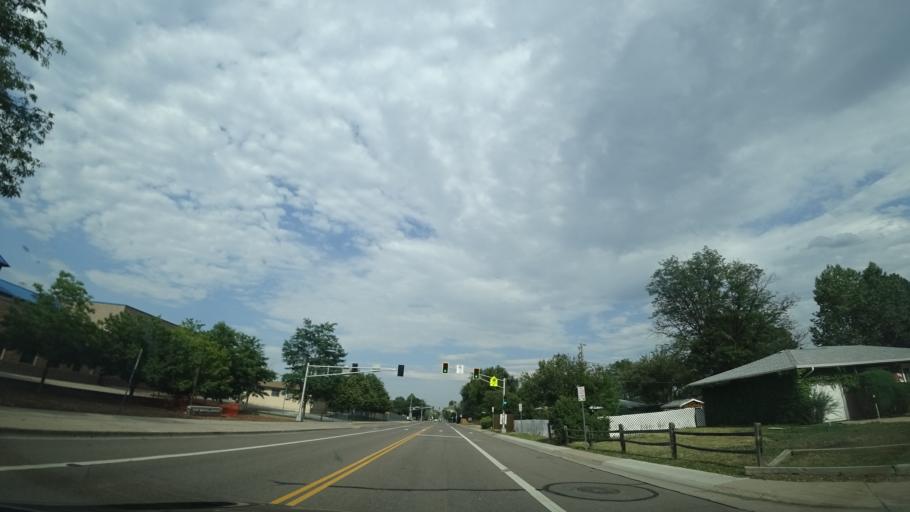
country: US
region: Colorado
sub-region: Jefferson County
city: Lakewood
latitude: 39.7185
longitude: -105.0929
